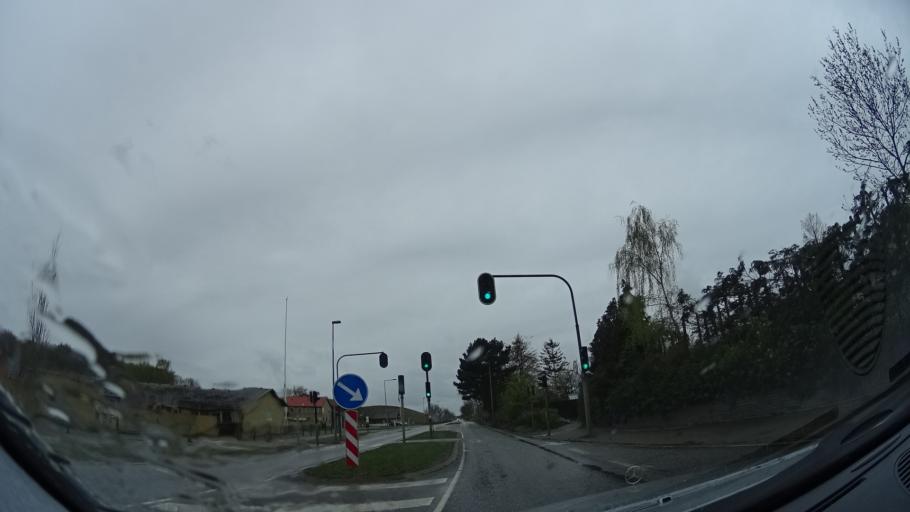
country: DK
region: Zealand
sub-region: Lejre Kommune
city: Ejby
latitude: 55.6848
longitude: 11.8471
